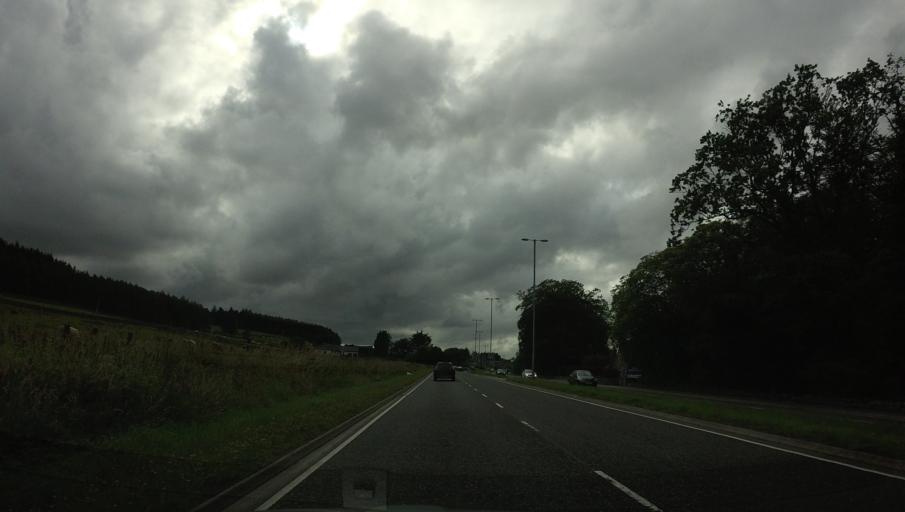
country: GB
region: Scotland
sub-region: Aberdeenshire
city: Westhill
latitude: 57.1464
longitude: -2.2291
